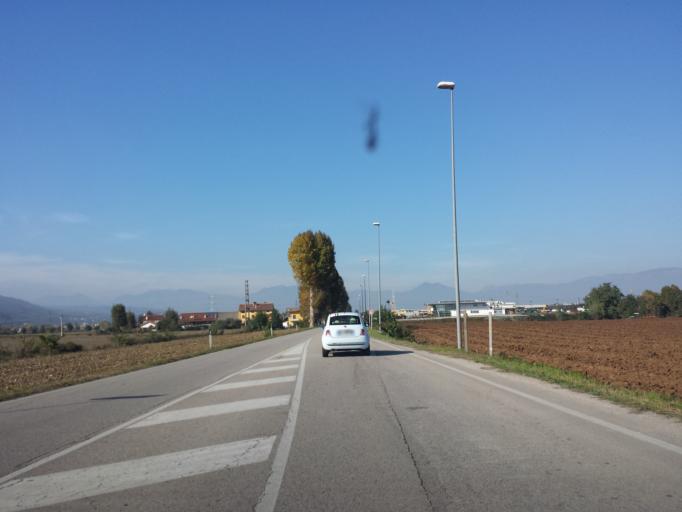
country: IT
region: Veneto
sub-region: Provincia di Vicenza
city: Crispi Cavour
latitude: 45.5825
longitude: 11.5060
